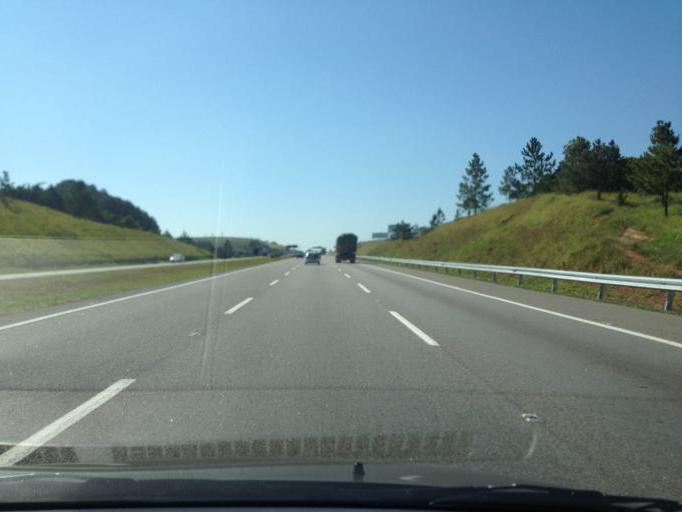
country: BR
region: Sao Paulo
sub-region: Guararema
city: Guararema
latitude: -23.3499
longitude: -46.0483
